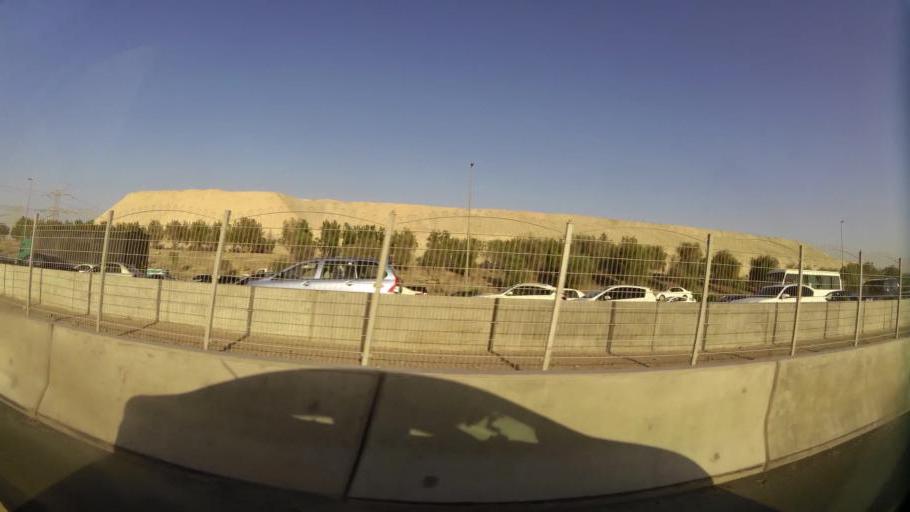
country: AE
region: Ash Shariqah
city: Sharjah
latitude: 25.2831
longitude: 55.4251
